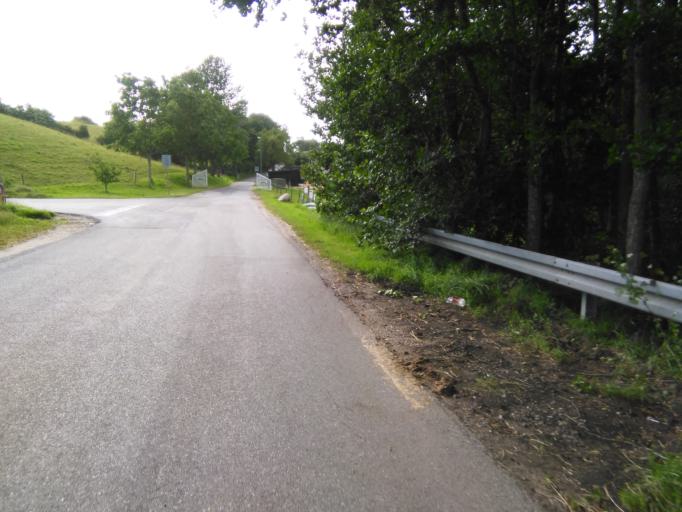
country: DK
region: Central Jutland
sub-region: Arhus Kommune
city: Beder
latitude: 56.0748
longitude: 10.2063
